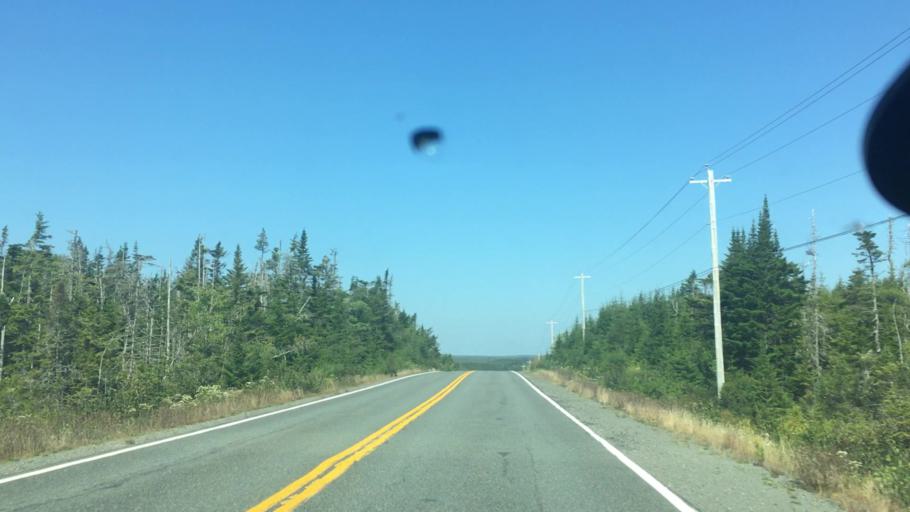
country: CA
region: Nova Scotia
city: Antigonish
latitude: 44.9911
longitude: -62.0962
